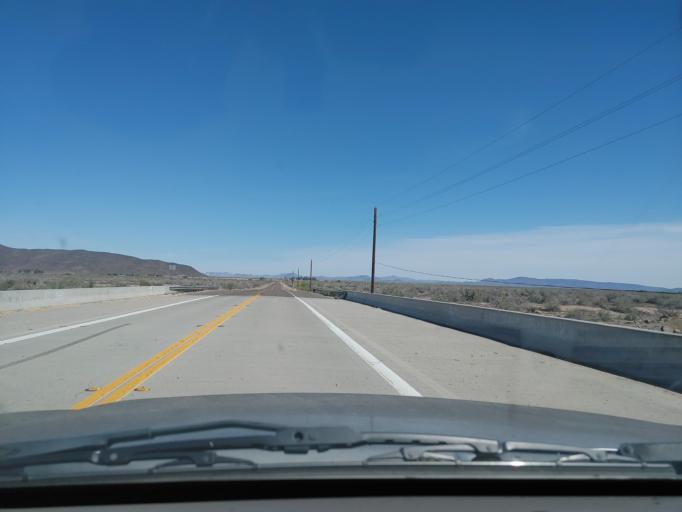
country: US
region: Arizona
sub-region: Maricopa County
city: Gila Bend
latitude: 32.9625
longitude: -113.3059
